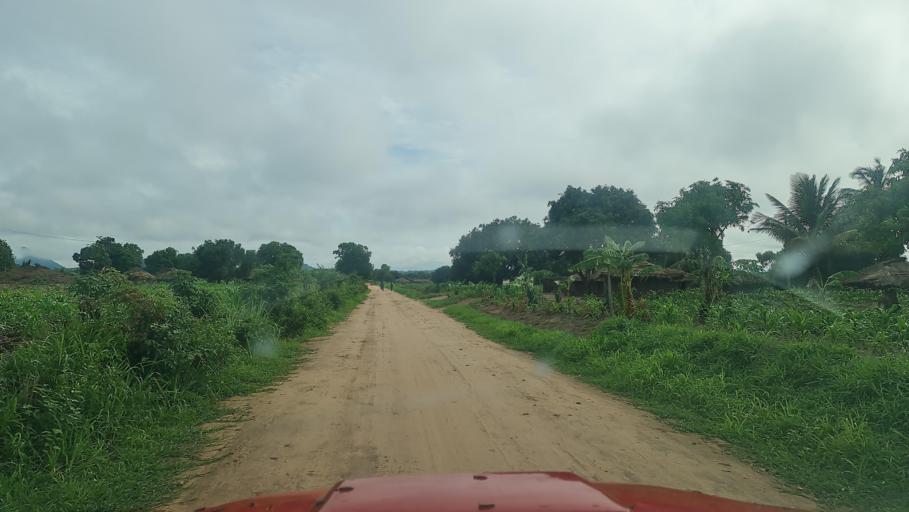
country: MW
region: Southern Region
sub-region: Nsanje District
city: Nsanje
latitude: -17.2886
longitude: 35.6050
